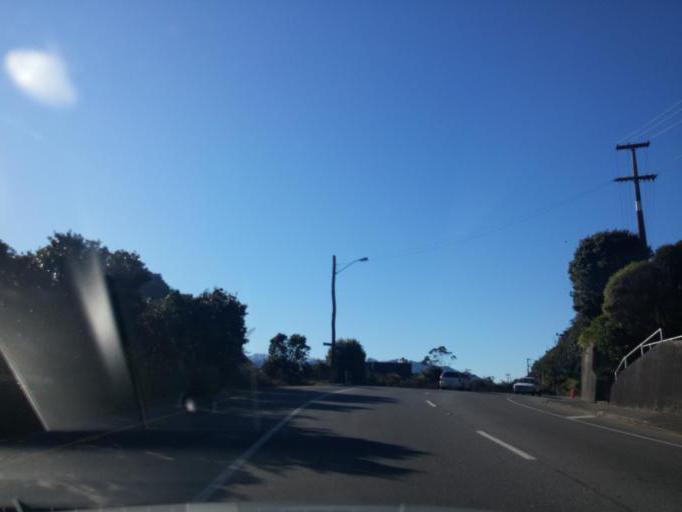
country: NZ
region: West Coast
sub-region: Grey District
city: Greymouth
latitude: -42.4495
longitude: 171.2132
